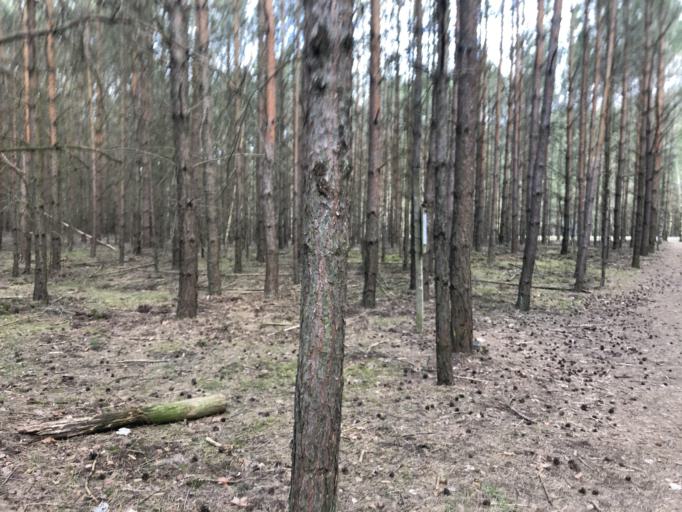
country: DE
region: Brandenburg
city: Hohen Neuendorf
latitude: 52.6594
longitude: 13.2971
